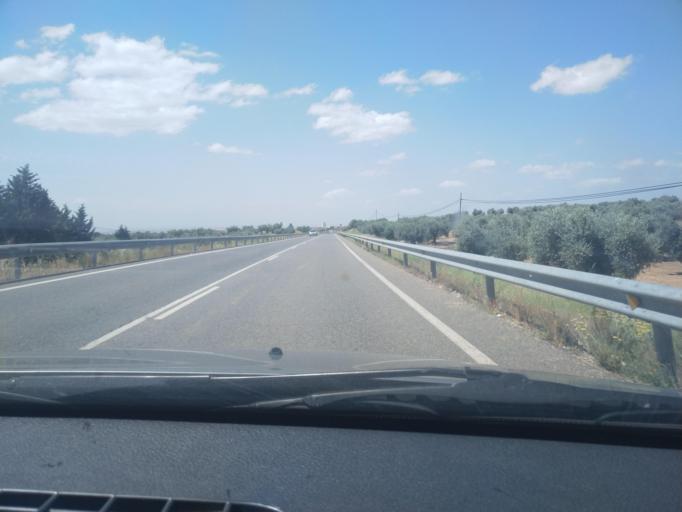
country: ES
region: Castille-La Mancha
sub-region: Province of Toledo
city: Polan
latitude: 39.7751
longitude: -4.1541
